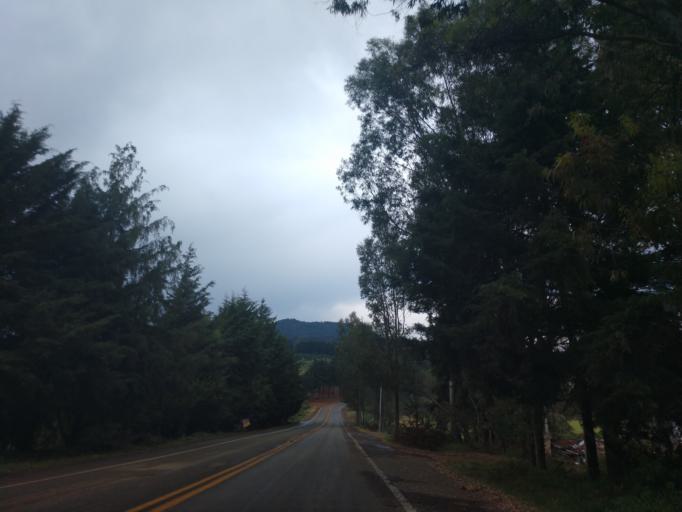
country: MX
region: Jalisco
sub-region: Mazamitla
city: Mazamitla
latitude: 19.9361
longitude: -103.0533
